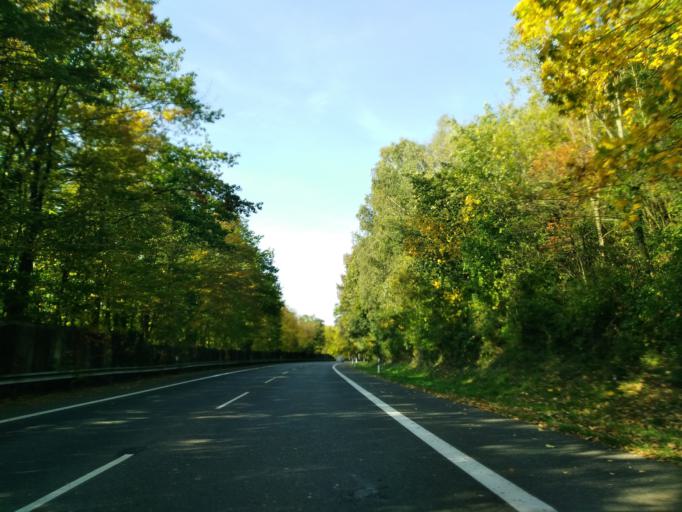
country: DE
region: North Rhine-Westphalia
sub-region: Regierungsbezirk Koln
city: Hennef
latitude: 50.7070
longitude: 7.2865
